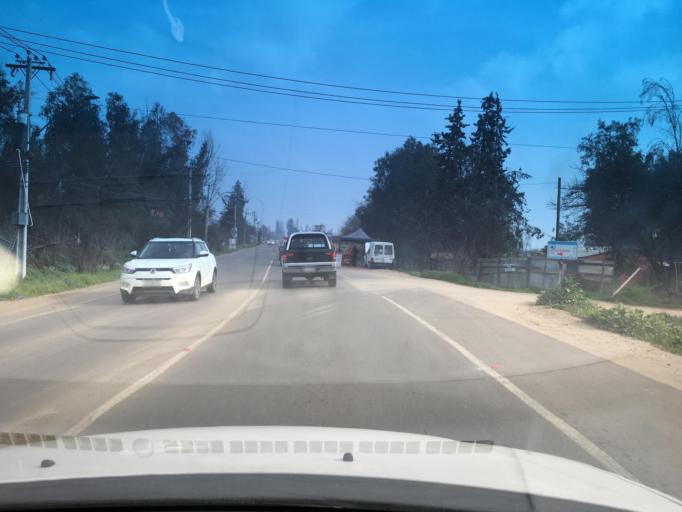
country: CL
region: Santiago Metropolitan
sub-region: Provincia de Chacabuco
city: Lampa
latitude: -33.3156
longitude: -70.8359
